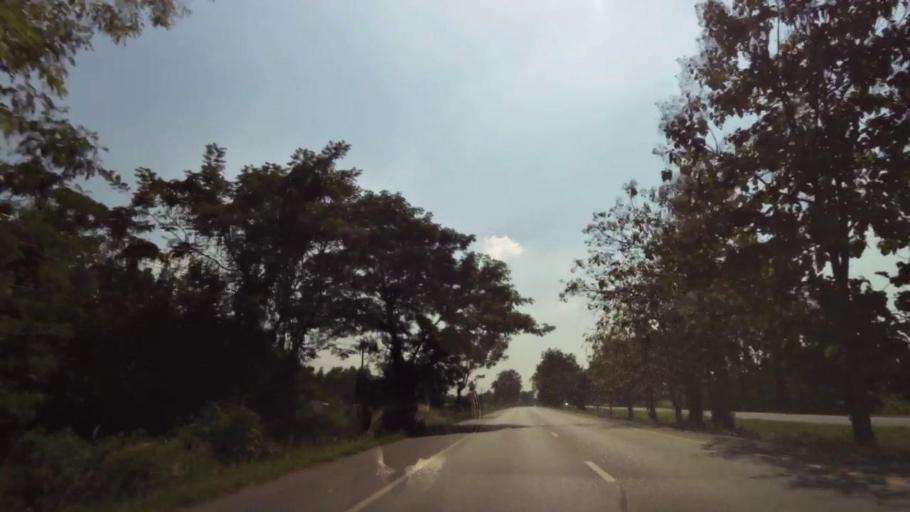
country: TH
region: Phichit
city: Bueng Na Rang
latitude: 16.1819
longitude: 100.1286
